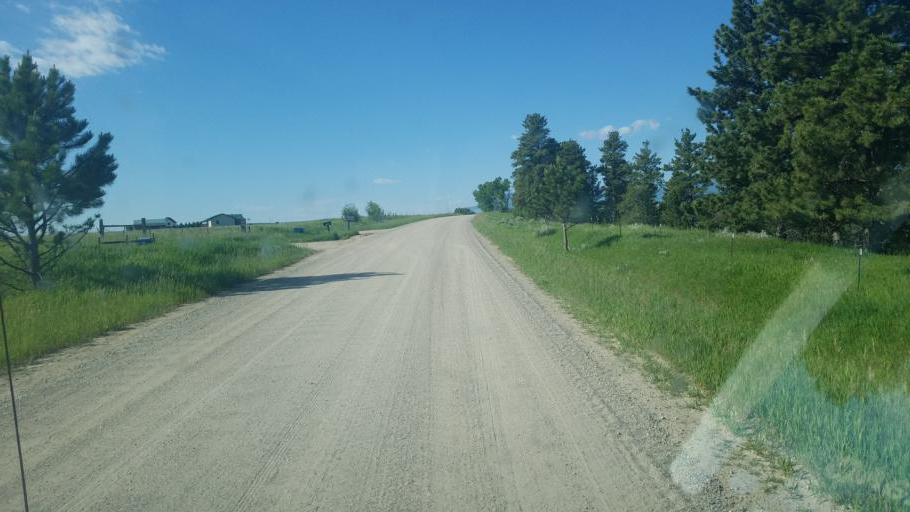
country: US
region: Montana
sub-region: Carbon County
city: Red Lodge
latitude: 45.3562
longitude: -109.1591
